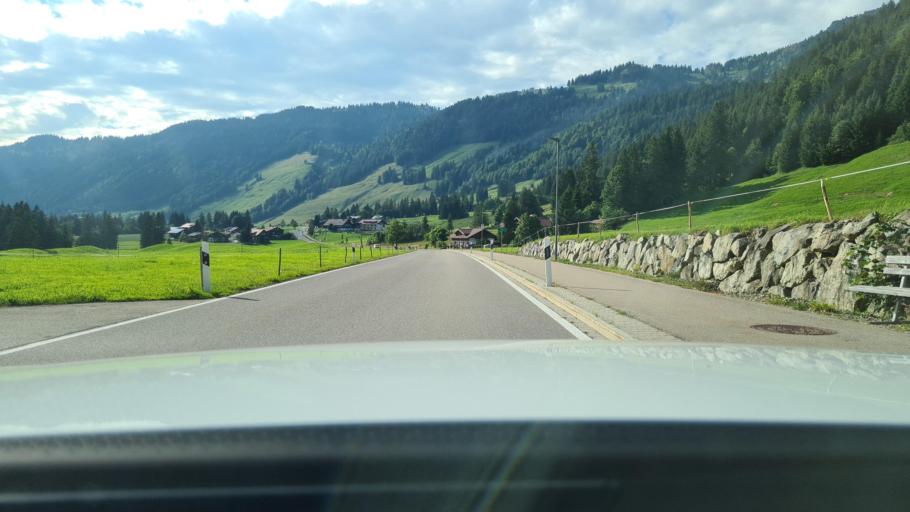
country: DE
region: Bavaria
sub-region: Swabia
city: Balderschwang
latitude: 47.4595
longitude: 10.1272
